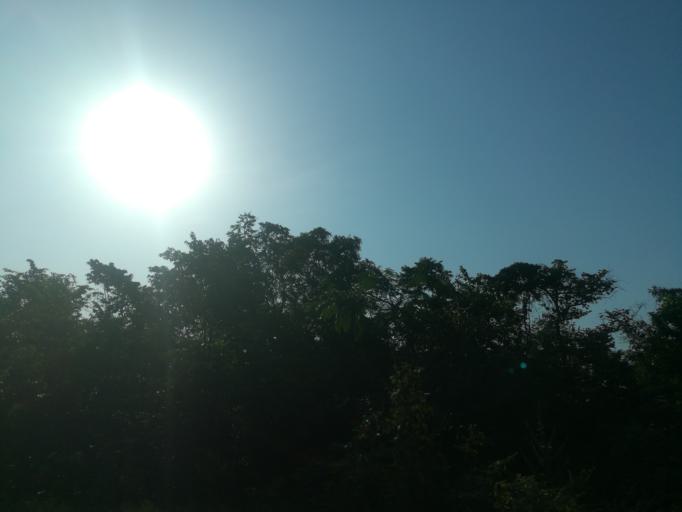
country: NG
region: Ogun
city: Abeokuta
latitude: 7.2529
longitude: 3.3004
